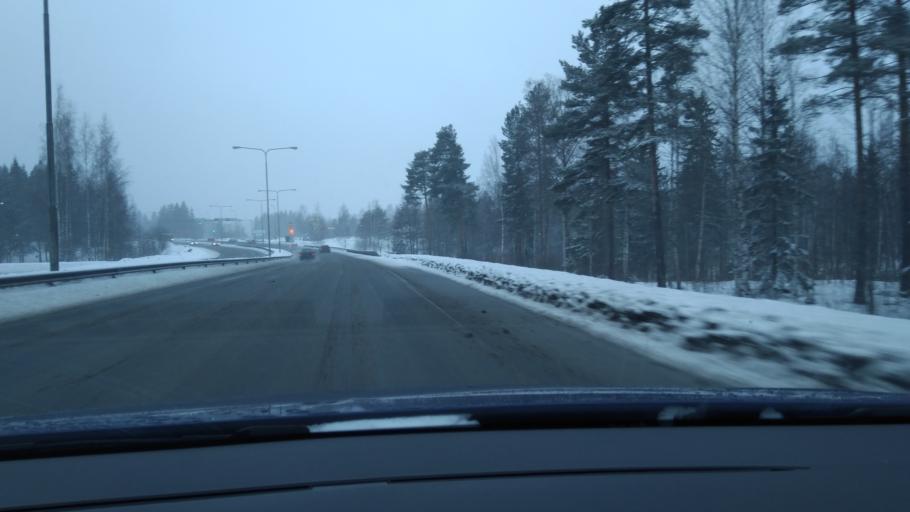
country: FI
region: Pirkanmaa
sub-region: Tampere
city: Tampere
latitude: 61.5025
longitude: 23.8656
